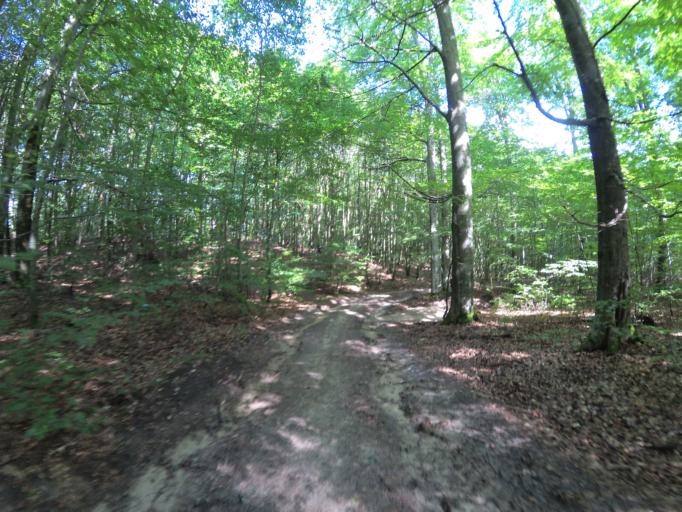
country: PL
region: Pomeranian Voivodeship
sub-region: Gdynia
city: Wielki Kack
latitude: 54.5083
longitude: 18.4488
